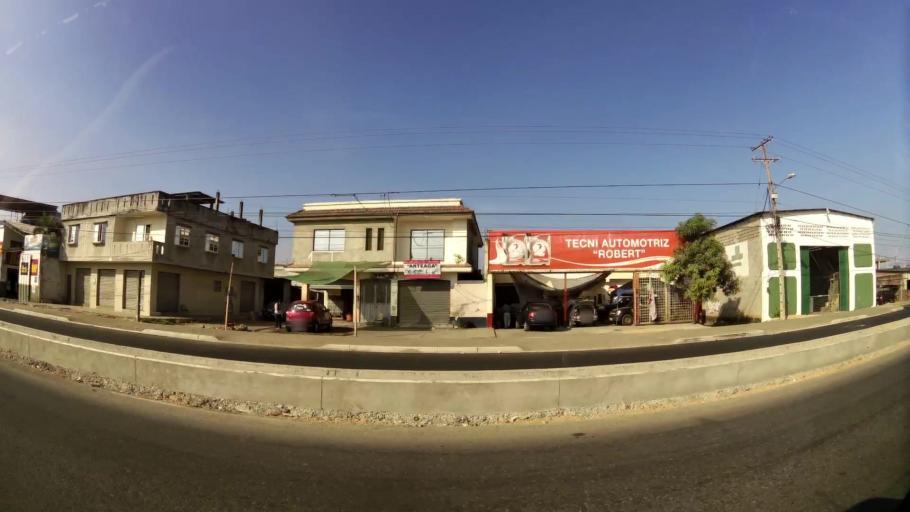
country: EC
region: Guayas
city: Eloy Alfaro
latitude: -2.1802
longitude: -79.8469
